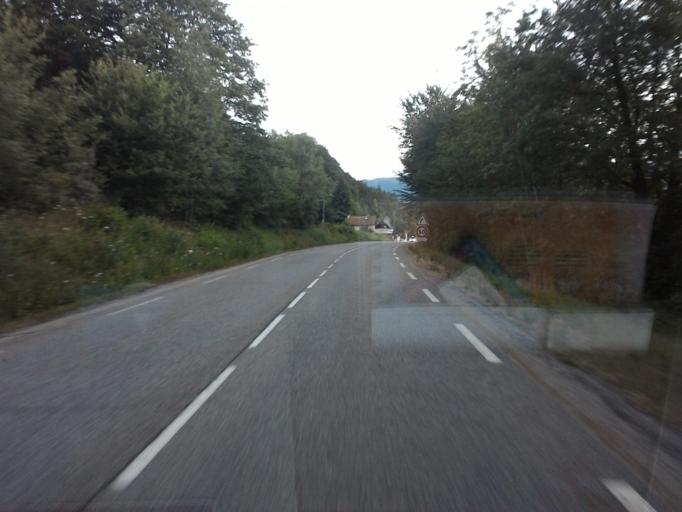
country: FR
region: Provence-Alpes-Cote d'Azur
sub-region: Departement des Hautes-Alpes
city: Saint-Bonnet-en-Champsaur
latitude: 44.7327
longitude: 6.0045
